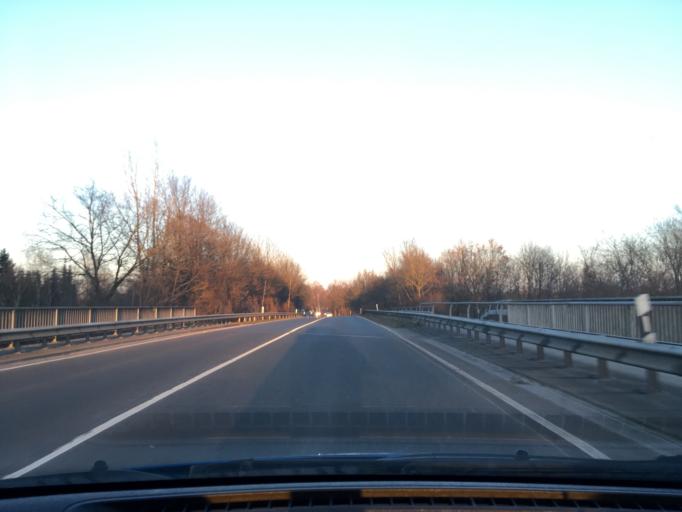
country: DE
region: Lower Saxony
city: Oyten
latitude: 53.0589
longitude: 8.9784
